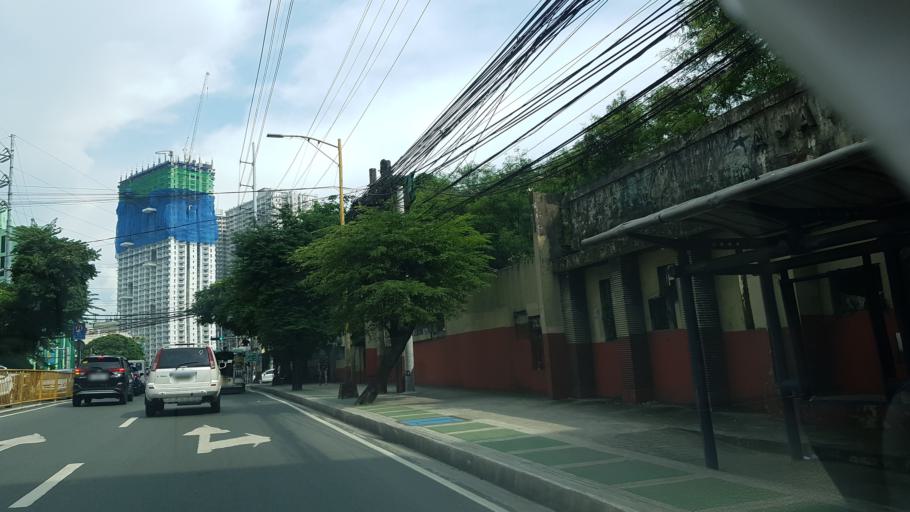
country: PH
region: Metro Manila
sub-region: Pasig
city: Pasig City
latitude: 14.5724
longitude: 121.0639
